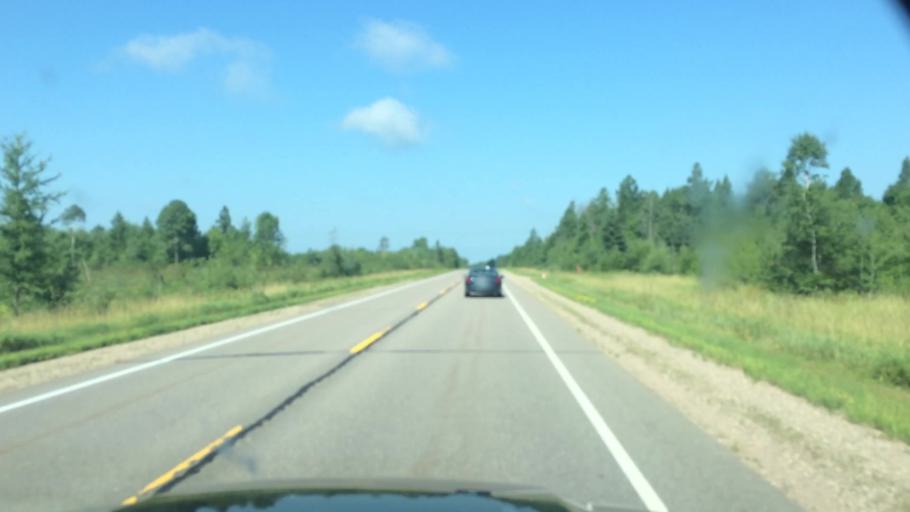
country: US
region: Wisconsin
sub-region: Langlade County
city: Antigo
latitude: 45.1450
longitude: -89.3127
